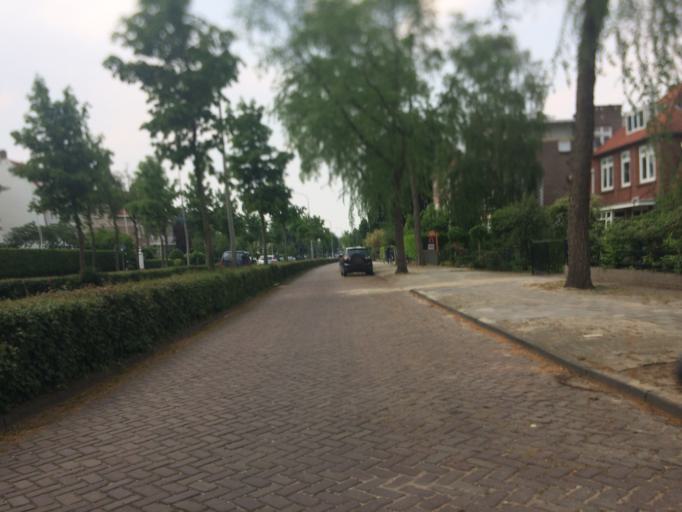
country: NL
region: Gelderland
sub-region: Gemeente Nijmegen
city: Nijmegen
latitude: 51.8316
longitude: 5.8734
